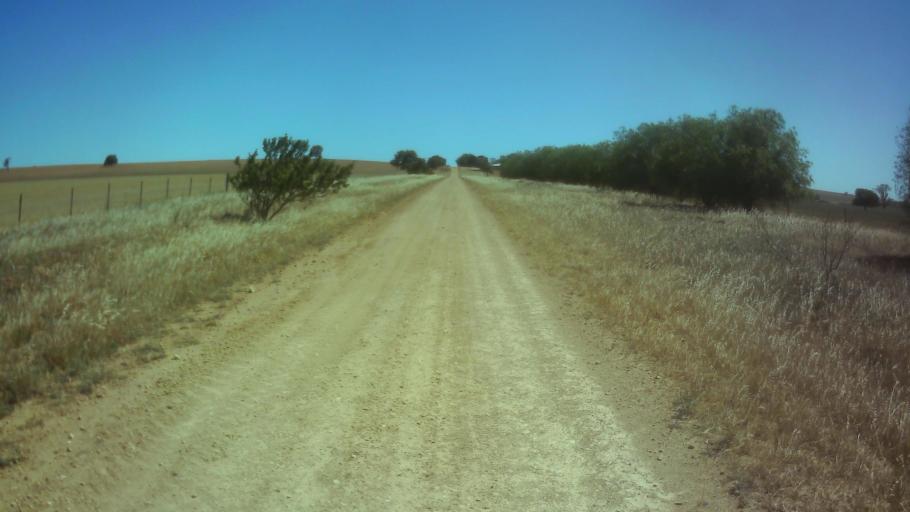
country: AU
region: New South Wales
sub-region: Weddin
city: Grenfell
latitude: -33.9909
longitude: 148.3573
